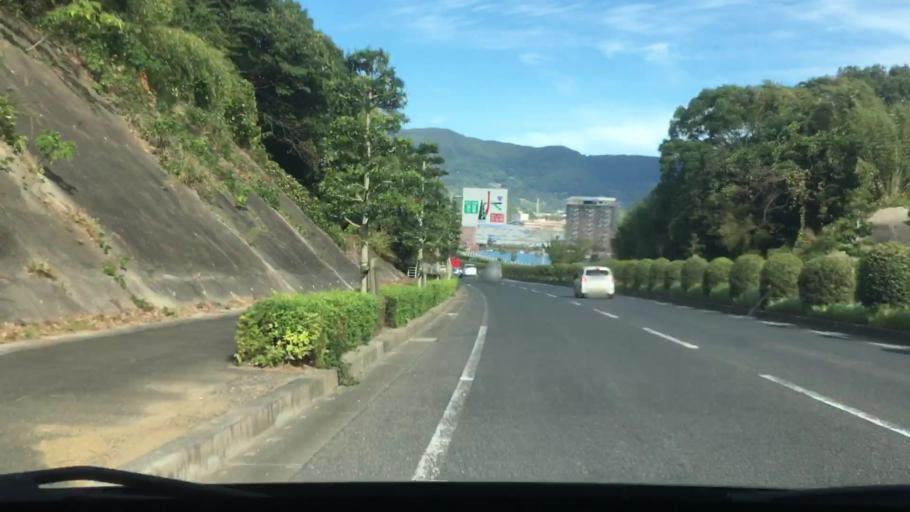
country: JP
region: Nagasaki
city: Sasebo
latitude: 33.1386
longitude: 129.7851
